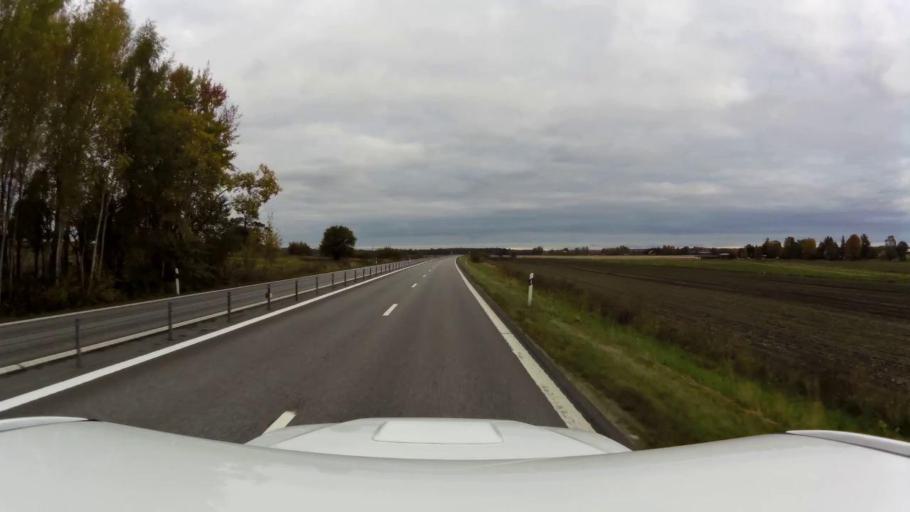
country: SE
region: OEstergoetland
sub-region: Linkopings Kommun
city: Malmslatt
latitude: 58.4443
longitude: 15.5156
